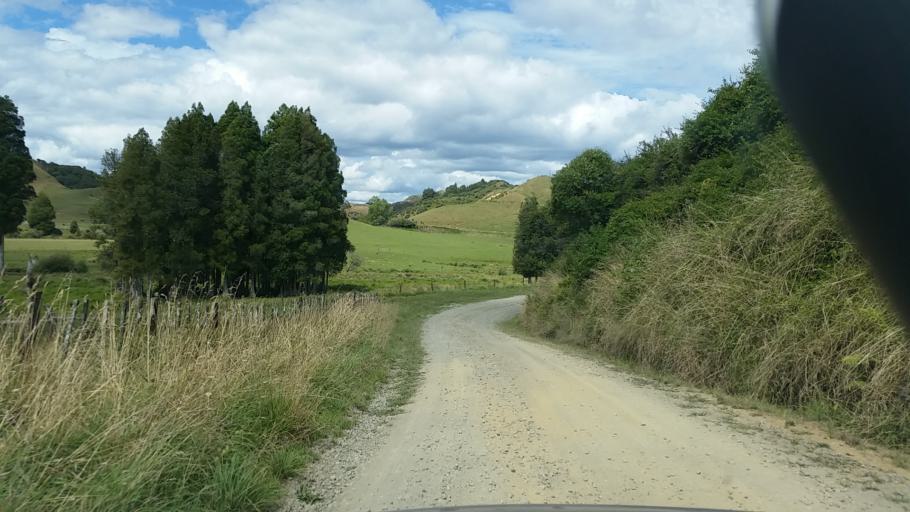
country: NZ
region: Taranaki
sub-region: South Taranaki District
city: Eltham
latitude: -39.2545
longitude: 174.5681
